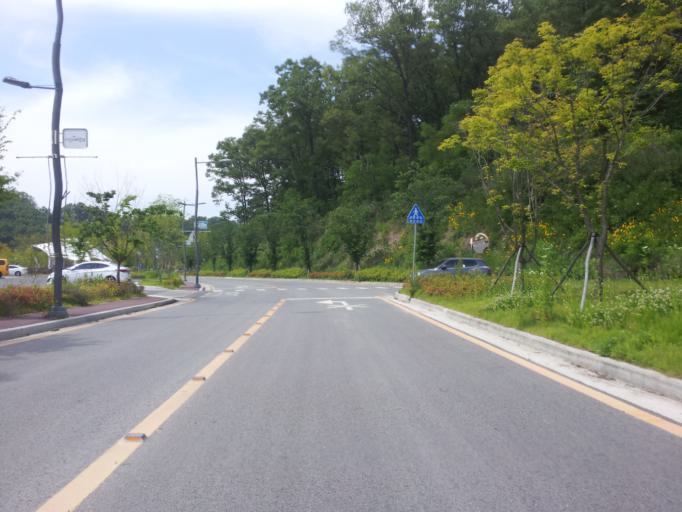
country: KR
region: Daejeon
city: Sintansin
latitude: 36.4548
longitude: 127.4759
